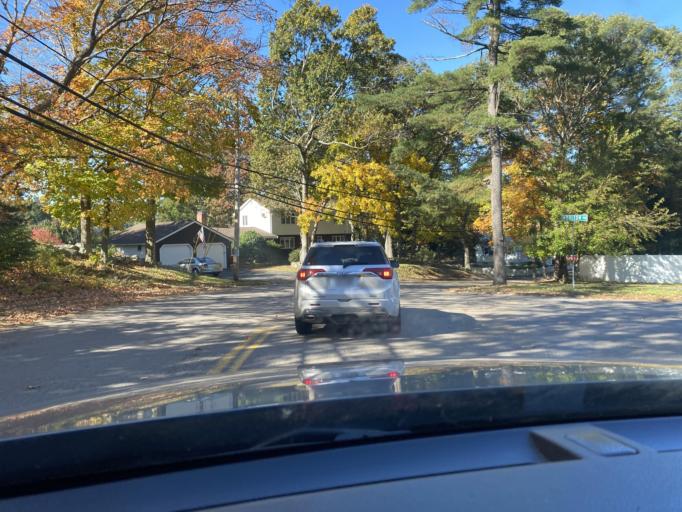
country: US
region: Massachusetts
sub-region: Essex County
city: South Peabody
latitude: 42.5359
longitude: -70.9942
